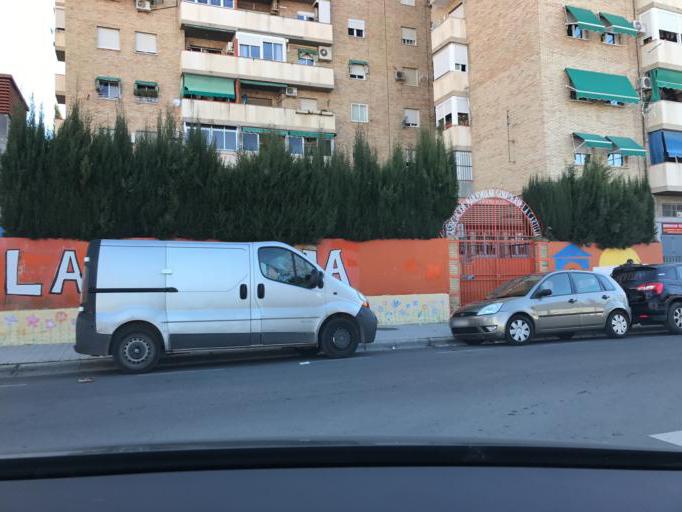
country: ES
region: Andalusia
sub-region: Provincia de Granada
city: Jun
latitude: 37.2046
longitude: -3.6003
